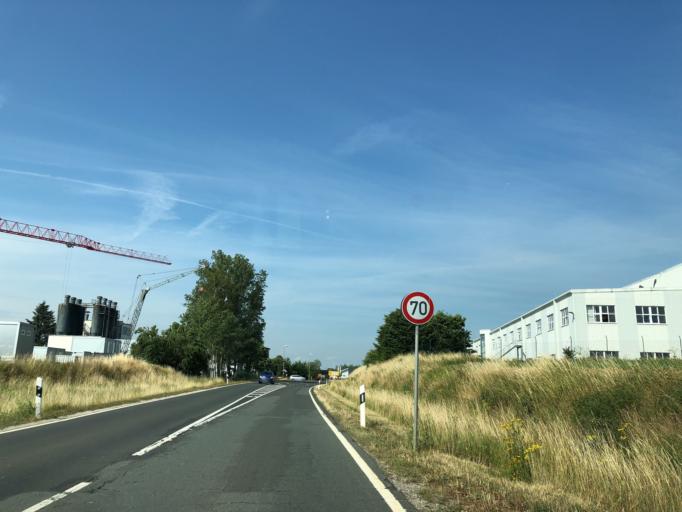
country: DE
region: Bavaria
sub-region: Regierungsbezirk Mittelfranken
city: Wachenroth
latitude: 49.7468
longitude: 10.6754
